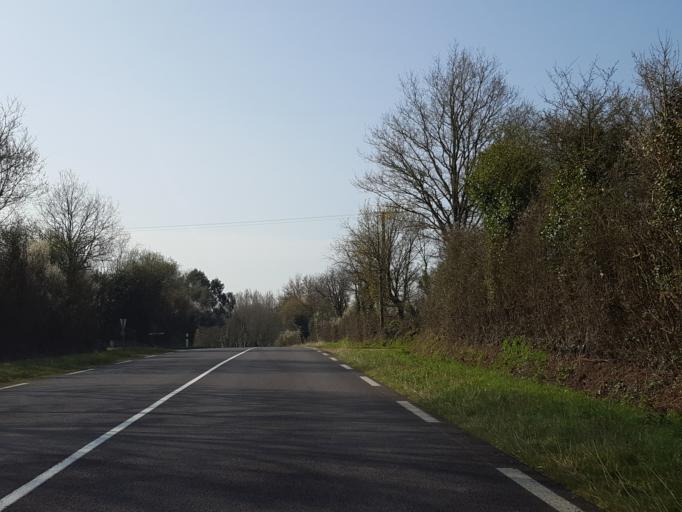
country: FR
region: Pays de la Loire
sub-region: Departement de la Vendee
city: Les Lucs-sur-Boulogne
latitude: 46.8645
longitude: -1.4987
